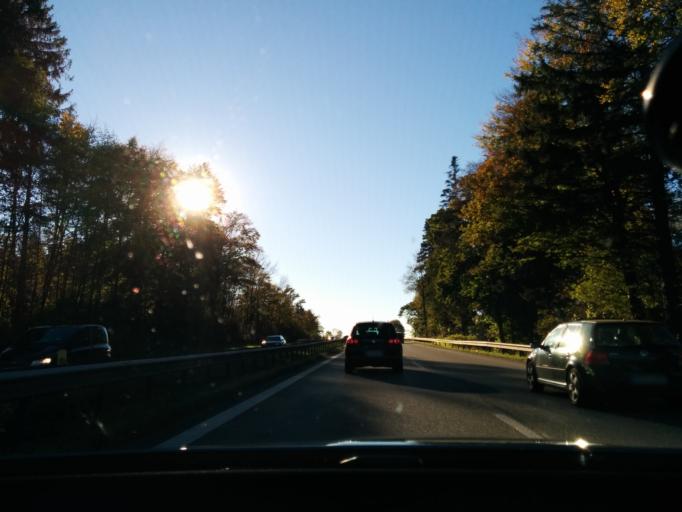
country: DE
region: Bavaria
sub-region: Upper Bavaria
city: Aschau im Chiemgau
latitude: 47.8059
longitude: 12.3305
